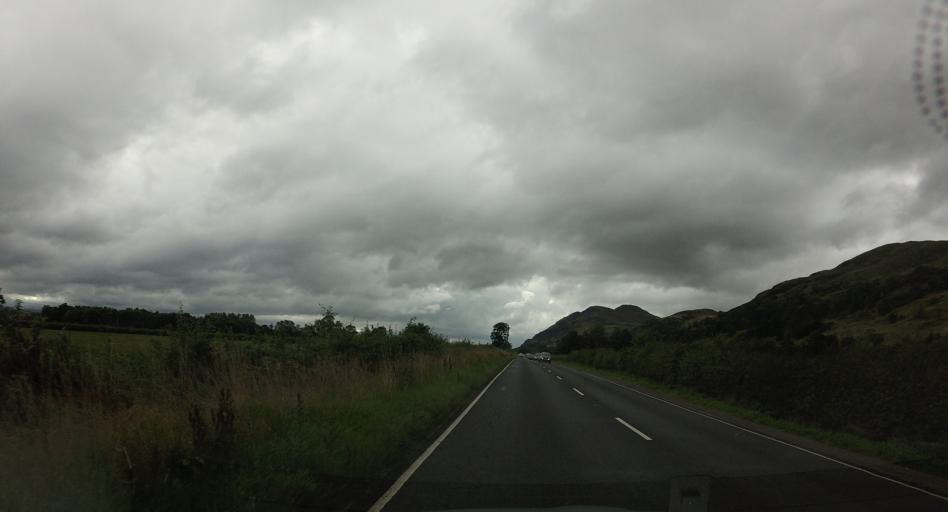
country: GB
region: Scotland
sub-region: Clackmannanshire
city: Alva
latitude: 56.1527
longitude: -3.8203
